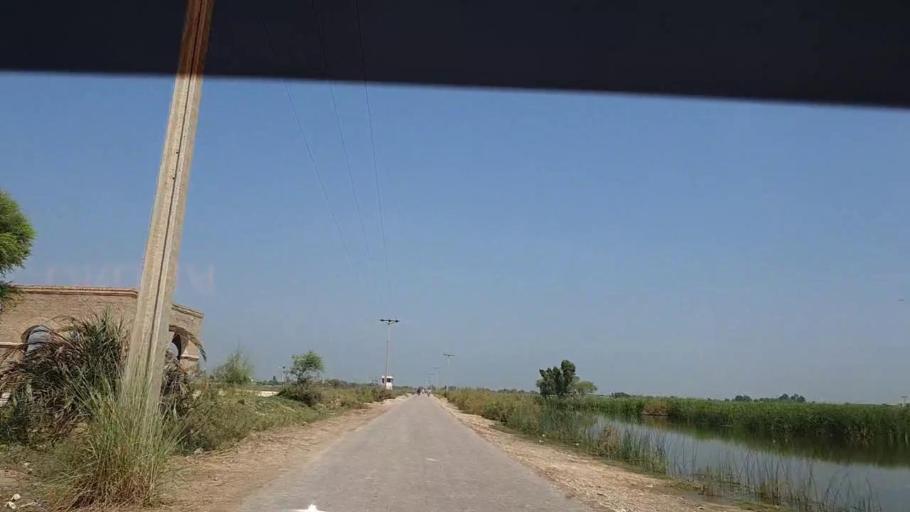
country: PK
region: Sindh
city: Tangwani
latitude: 28.2796
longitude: 69.0051
